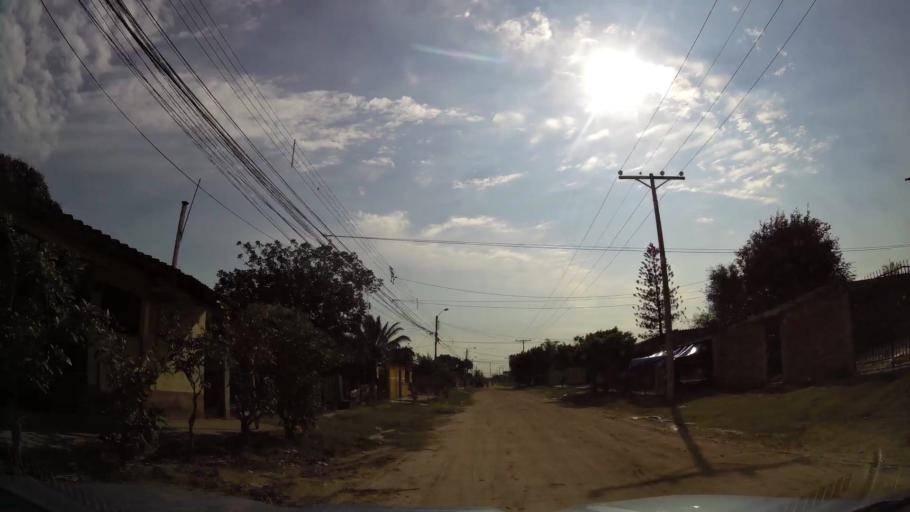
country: BO
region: Santa Cruz
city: Santa Cruz de la Sierra
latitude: -17.7348
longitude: -63.1427
